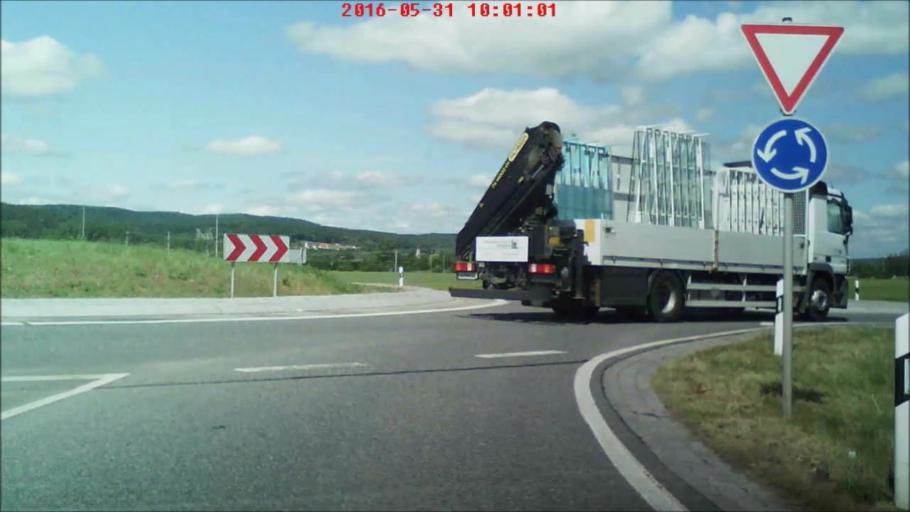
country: DE
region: Thuringia
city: Heldrungen
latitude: 51.3006
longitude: 11.2075
